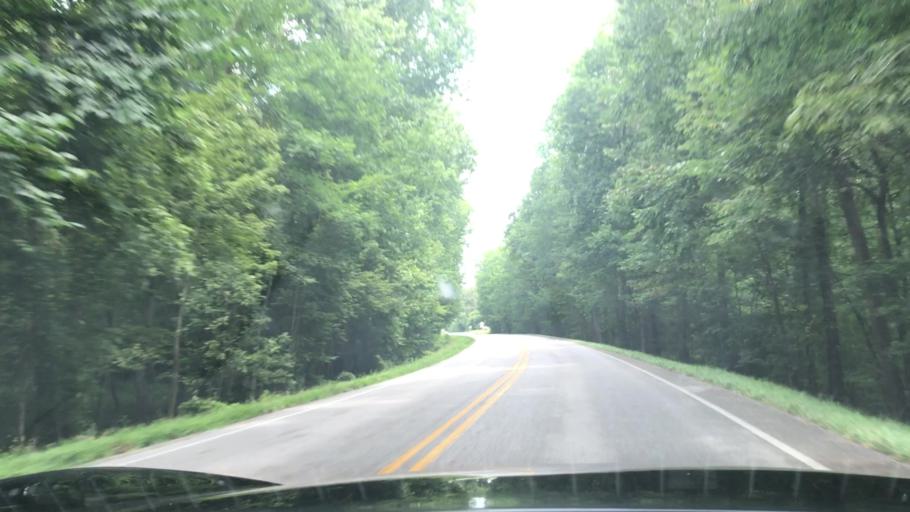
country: US
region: Kentucky
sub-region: Butler County
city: Morgantown
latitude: 37.1815
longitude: -86.7806
